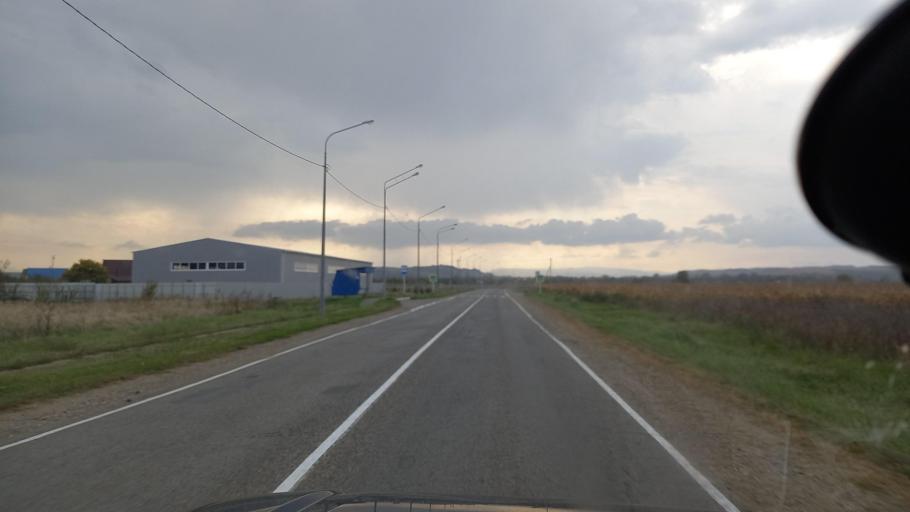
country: RU
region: Krasnodarskiy
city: Mostovskoy
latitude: 44.3942
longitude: 40.7686
